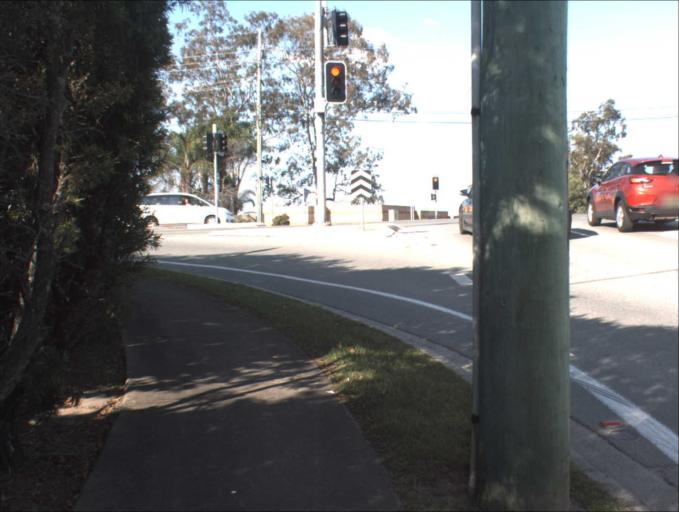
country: AU
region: Queensland
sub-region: Logan
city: Waterford West
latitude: -27.7016
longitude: 153.1584
